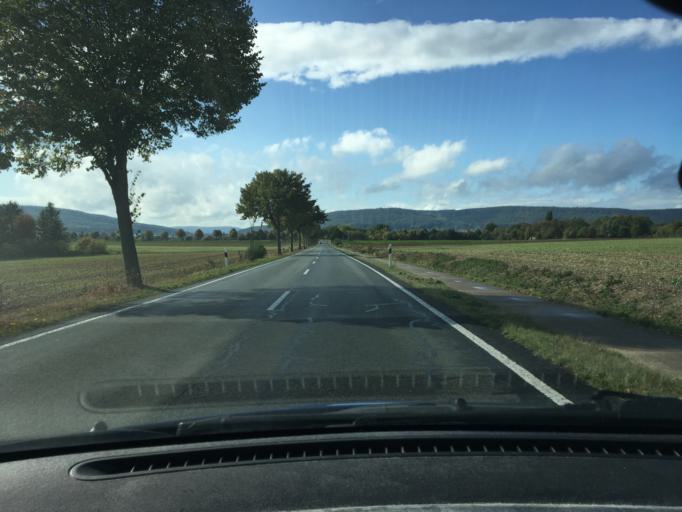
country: DE
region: Lower Saxony
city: Springe
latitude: 52.2114
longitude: 9.6008
